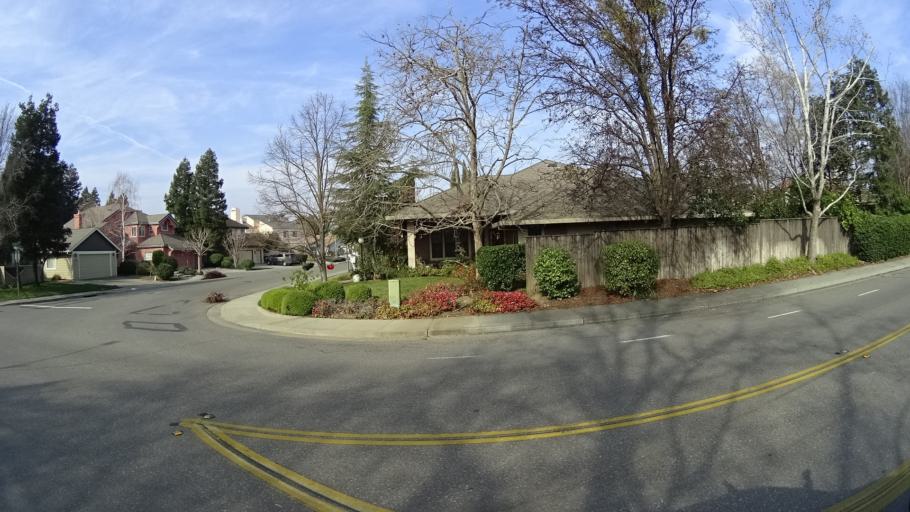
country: US
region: California
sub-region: Yolo County
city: Davis
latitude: 38.5734
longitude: -121.7546
